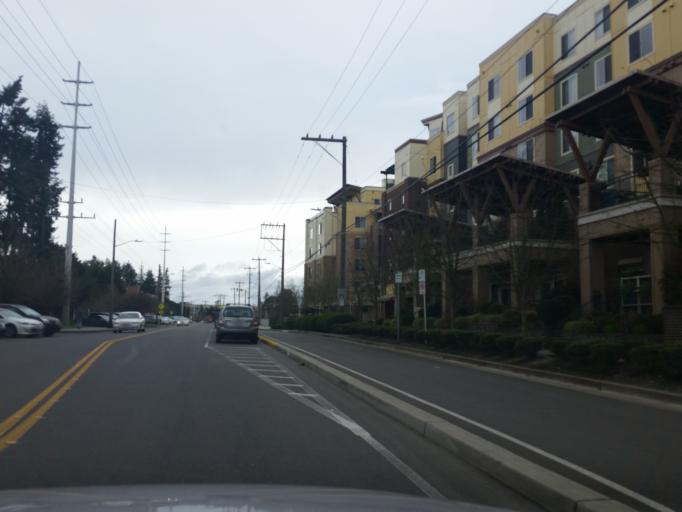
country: US
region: Washington
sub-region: King County
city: Shoreline
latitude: 47.7235
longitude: -122.3481
